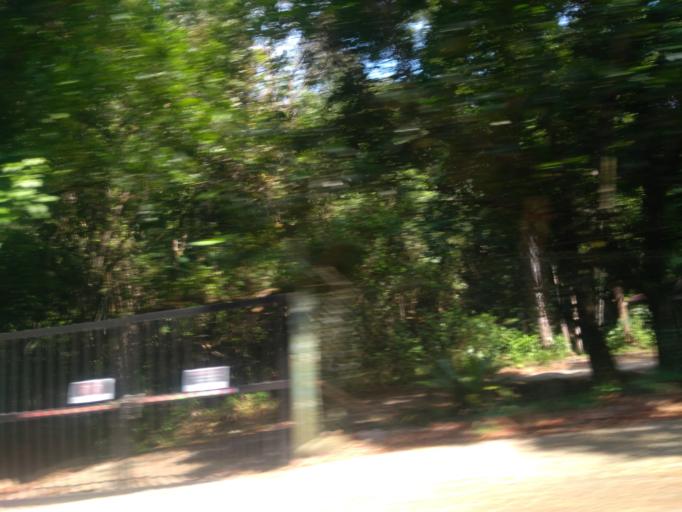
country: MY
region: Sarawak
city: Kuching
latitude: 1.7477
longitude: 110.3154
